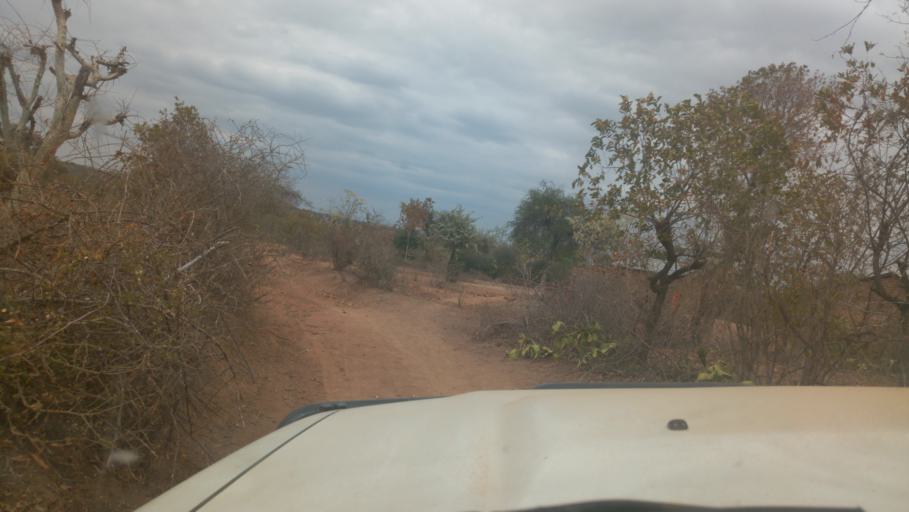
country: KE
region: Kitui
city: Kitui
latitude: -1.5890
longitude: 37.9304
